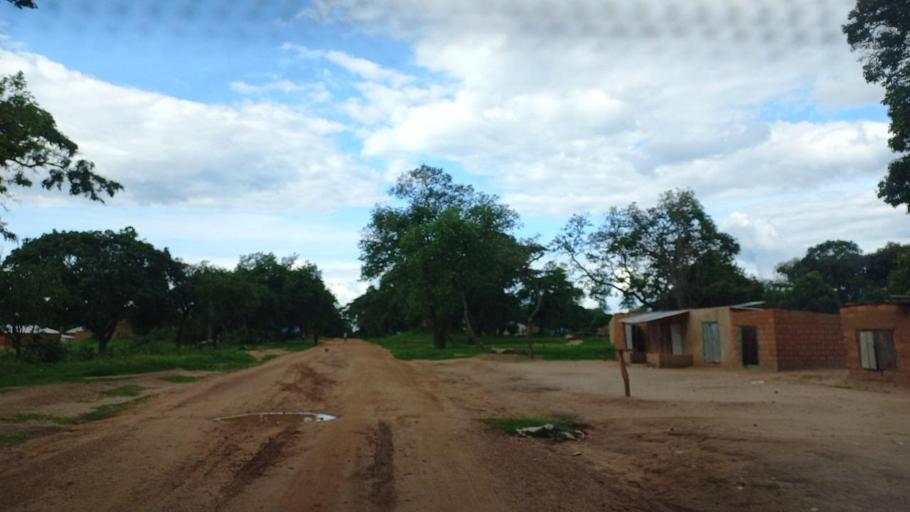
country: ZM
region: North-Western
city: Mwinilunga
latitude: -11.8439
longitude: 24.3642
